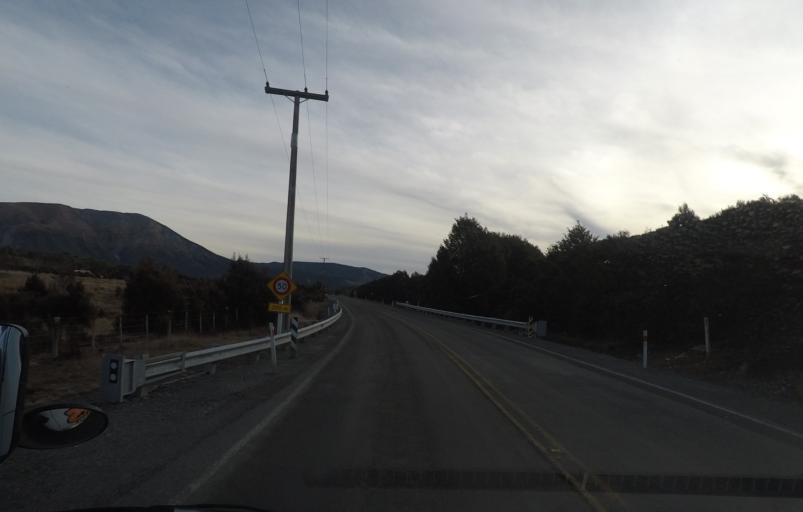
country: NZ
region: Tasman
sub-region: Tasman District
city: Wakefield
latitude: -41.8000
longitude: 172.8615
